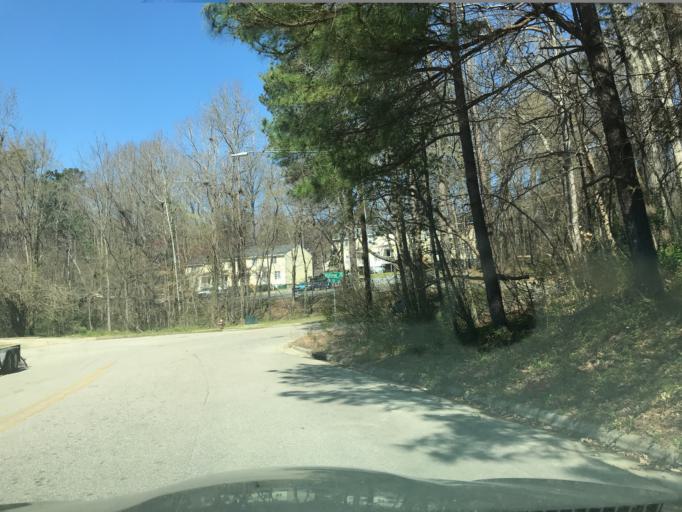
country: US
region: North Carolina
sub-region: Wake County
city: Raleigh
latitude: 35.8446
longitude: -78.5983
